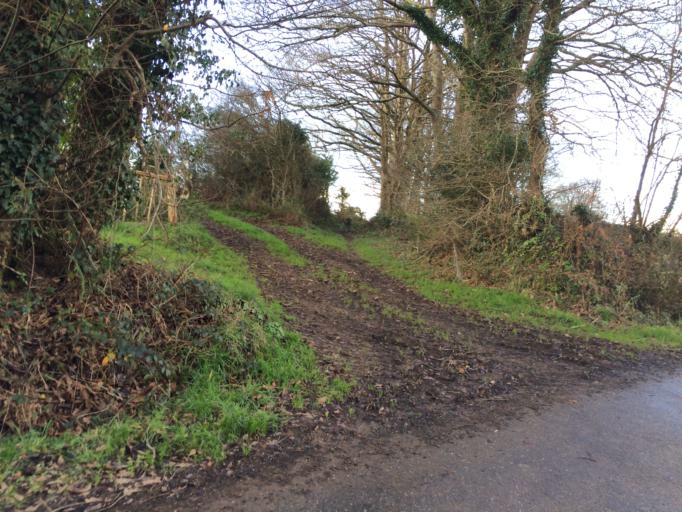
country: FR
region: Brittany
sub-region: Departement du Finistere
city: Daoulas
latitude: 48.3344
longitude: -4.2705
